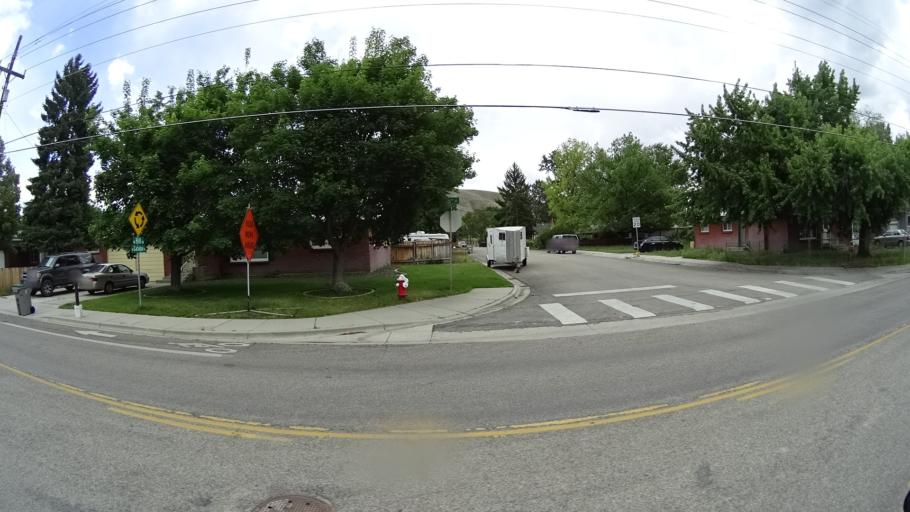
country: US
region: Idaho
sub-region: Ada County
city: Garden City
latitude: 43.6539
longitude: -116.2334
